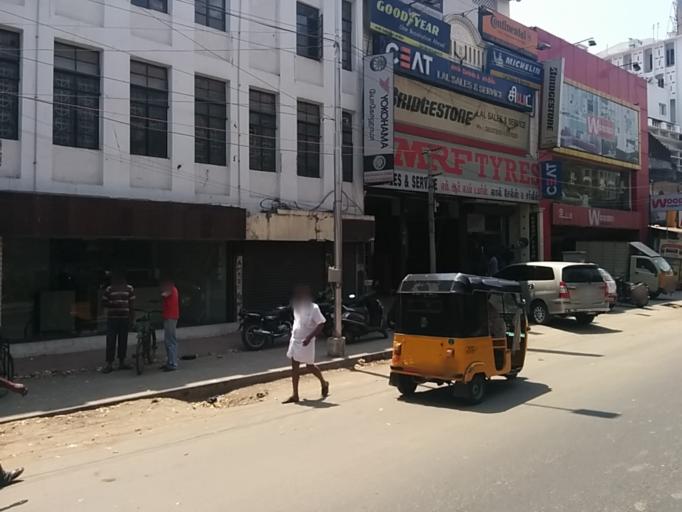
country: IN
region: Tamil Nadu
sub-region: Chennai
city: Chetput
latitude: 13.0571
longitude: 80.2598
